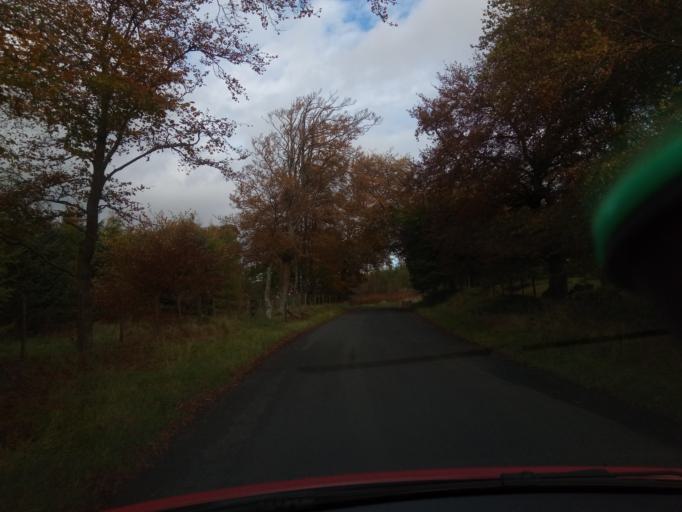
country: GB
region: Scotland
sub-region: South Lanarkshire
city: Carnwath
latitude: 55.7419
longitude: -3.6042
